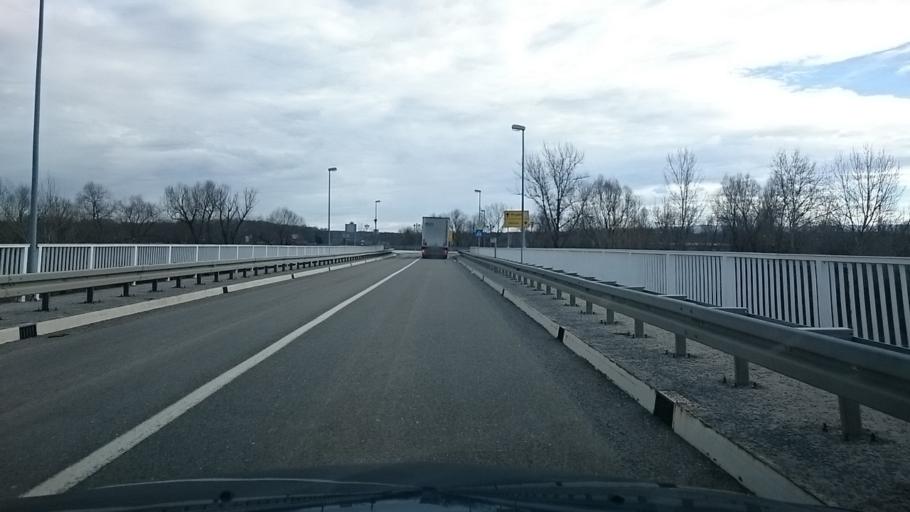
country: HR
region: Sisacko-Moslavacka
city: Novska
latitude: 45.2687
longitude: 16.9154
